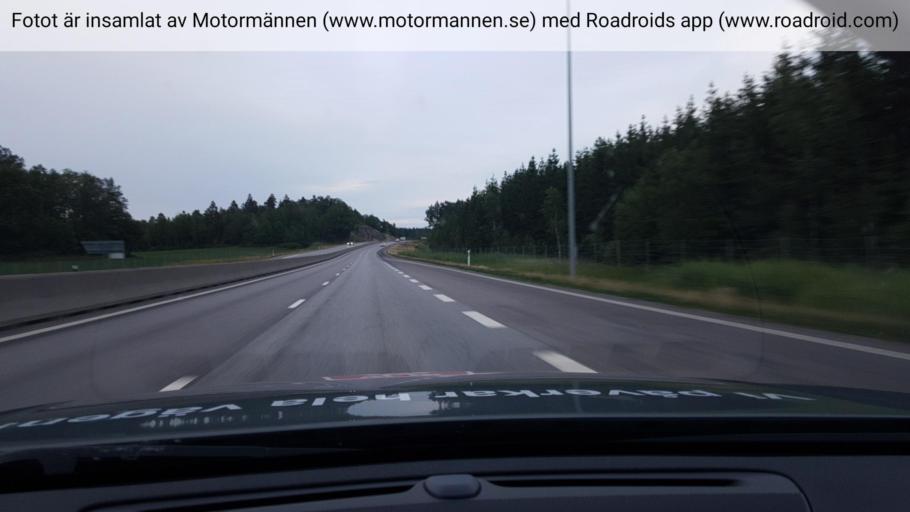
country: SE
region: OEstergoetland
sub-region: Norrkopings Kommun
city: Kimstad
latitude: 58.5275
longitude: 16.0143
